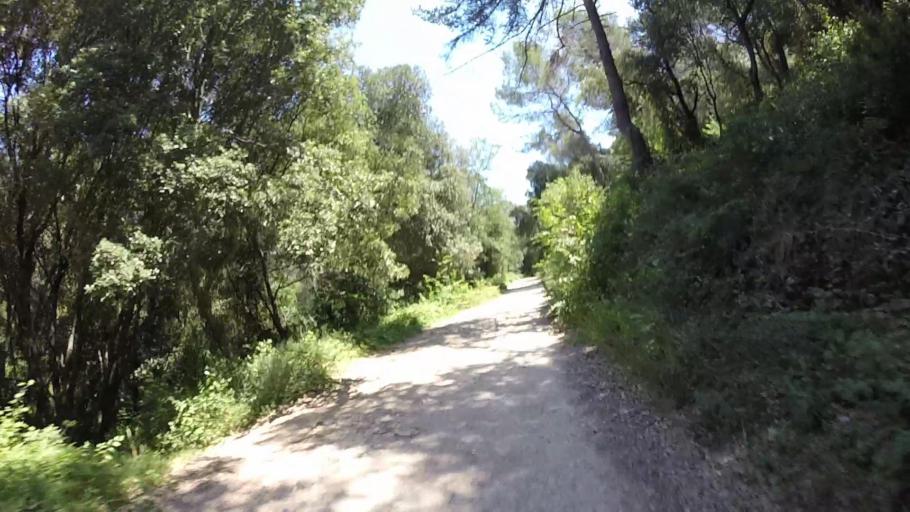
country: FR
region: Provence-Alpes-Cote d'Azur
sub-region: Departement des Alpes-Maritimes
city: Mougins
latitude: 43.5996
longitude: 7.0256
